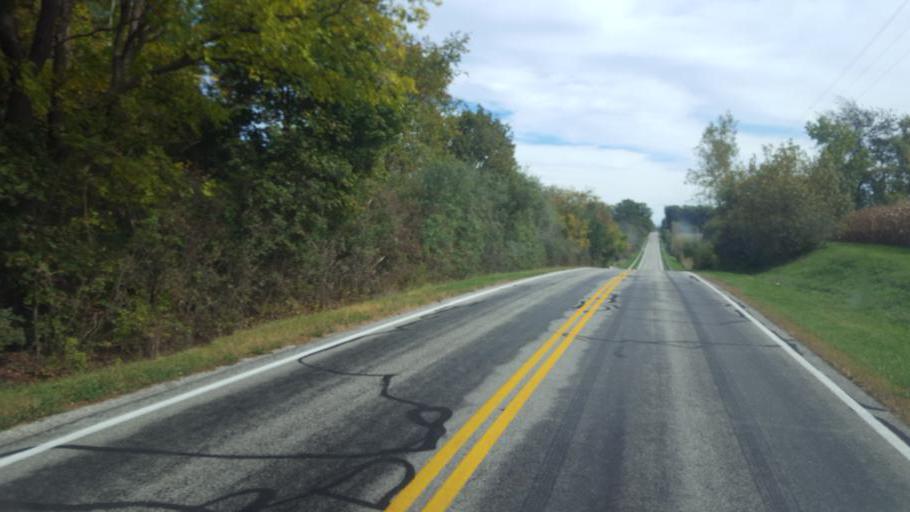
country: US
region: Ohio
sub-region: Erie County
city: Huron
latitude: 41.3649
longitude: -82.5093
